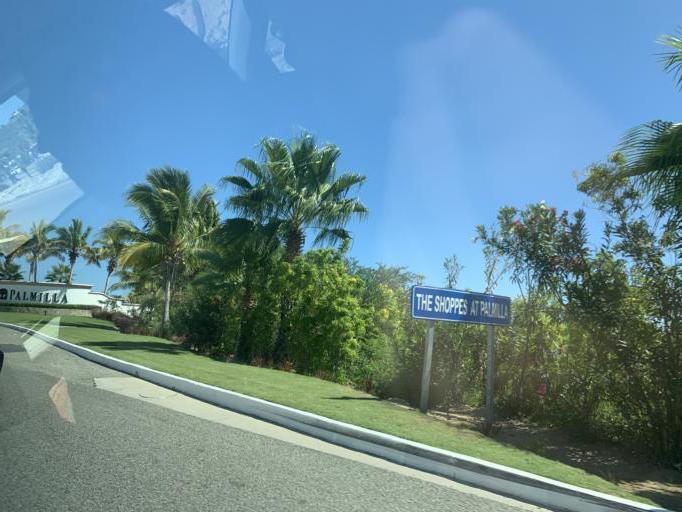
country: MX
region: Baja California Sur
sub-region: Los Cabos
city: San Jose del Cabo
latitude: 23.0121
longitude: -109.7232
